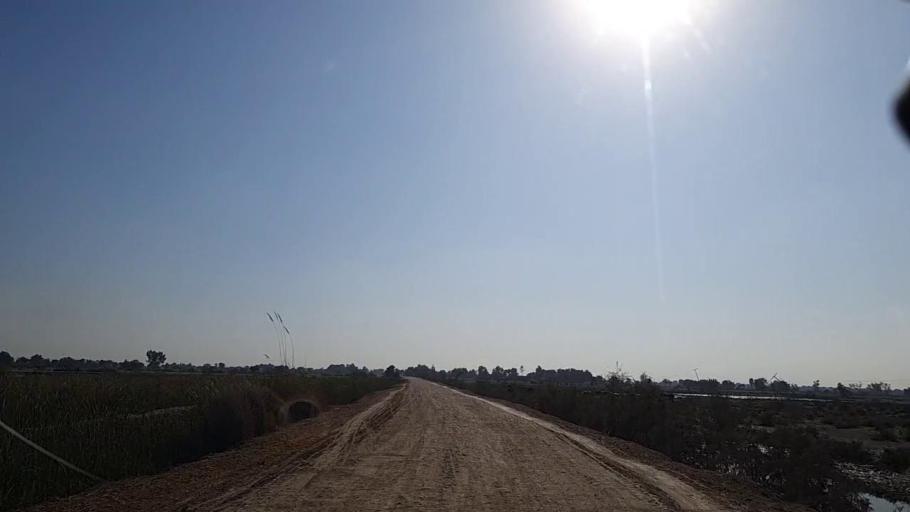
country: PK
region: Sindh
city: Khanpur
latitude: 27.7941
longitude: 69.3714
